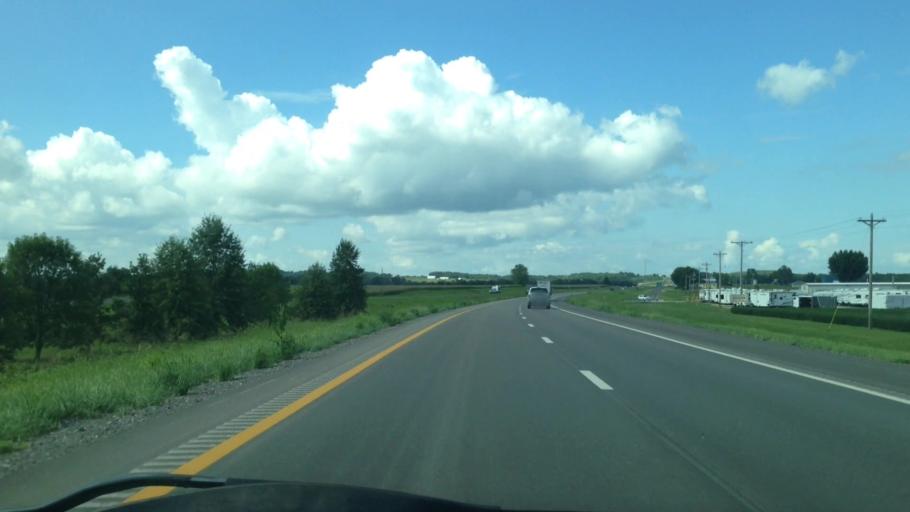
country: US
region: Illinois
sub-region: Adams County
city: Quincy
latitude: 39.9843
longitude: -91.5263
